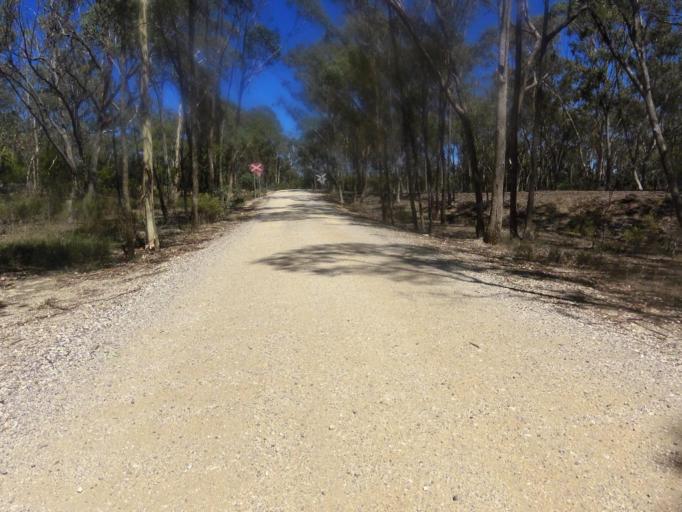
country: AU
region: Victoria
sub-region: Mount Alexander
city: Castlemaine
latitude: -37.0461
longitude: 144.1817
